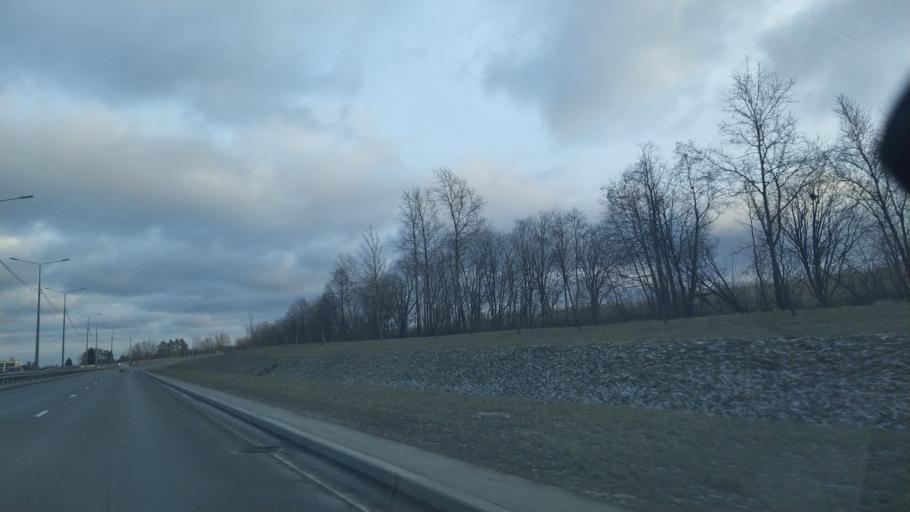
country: RU
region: St.-Petersburg
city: Aleksandrovskaya
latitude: 59.7725
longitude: 30.3392
